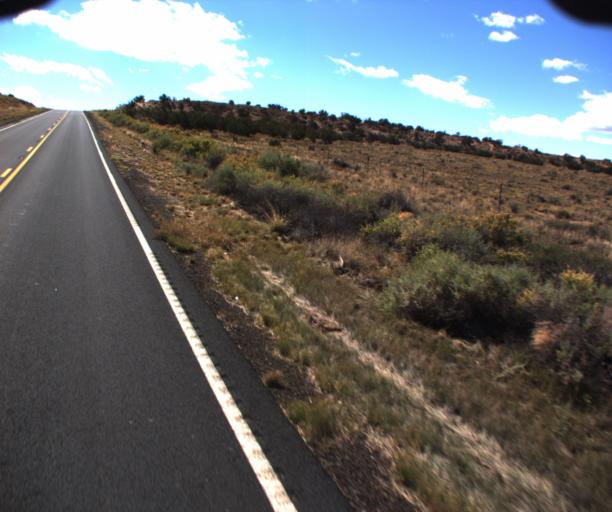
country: US
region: Arizona
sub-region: Apache County
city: Houck
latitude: 35.0917
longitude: -109.3116
